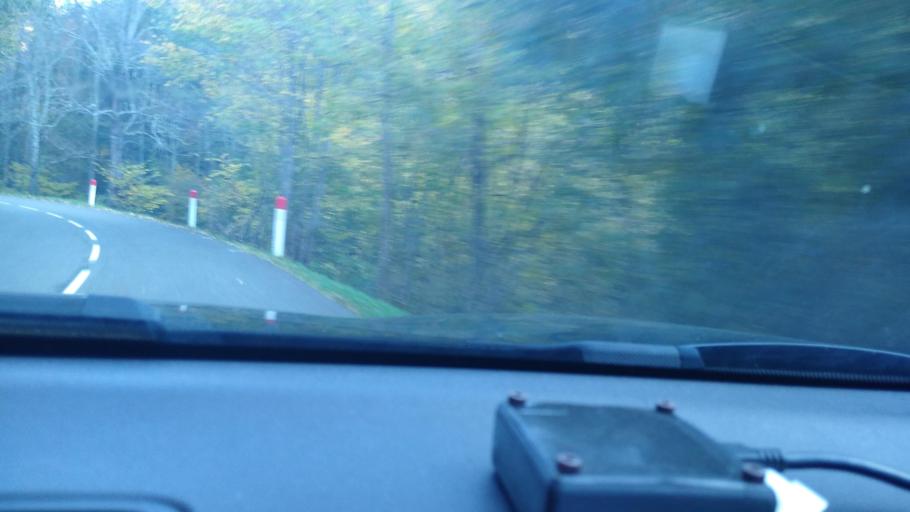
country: FR
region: Languedoc-Roussillon
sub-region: Departement de l'Aude
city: Quillan
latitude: 42.7273
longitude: 2.1098
